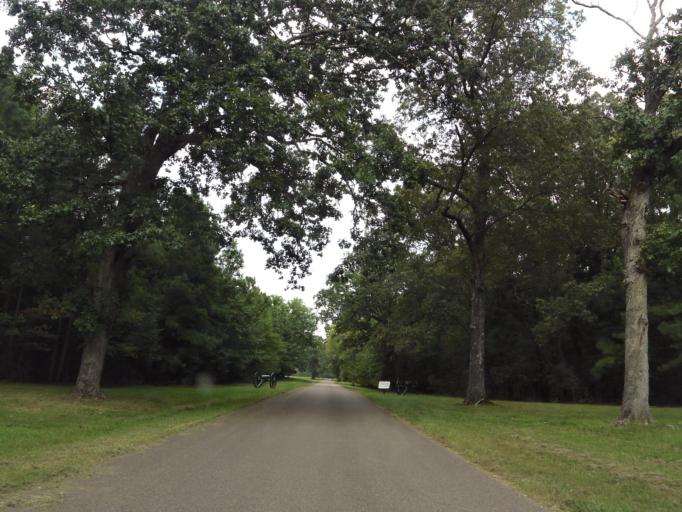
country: US
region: Tennessee
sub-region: Hardin County
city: Crump
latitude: 35.1261
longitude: -88.3403
